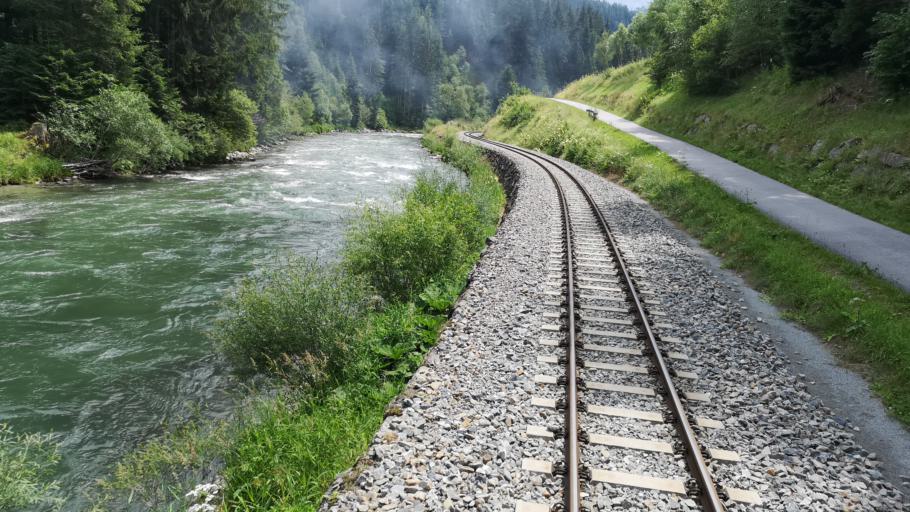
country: AT
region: Salzburg
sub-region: Politischer Bezirk Tamsweg
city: Tamsweg
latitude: 47.0971
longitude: 13.8207
